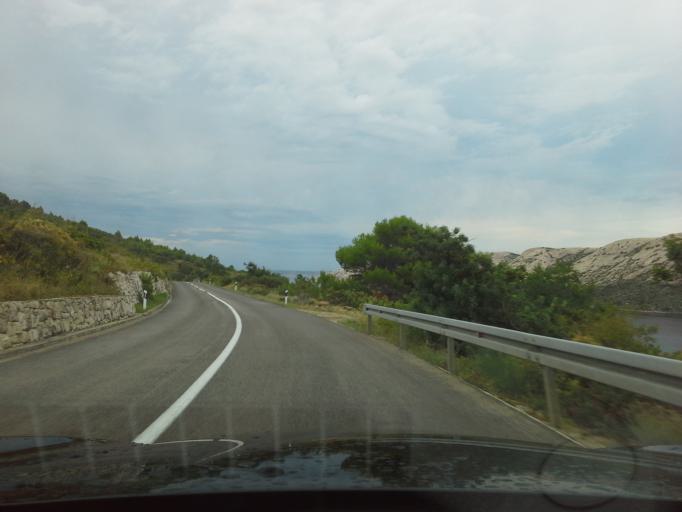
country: HR
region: Primorsko-Goranska
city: Banjol
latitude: 44.7170
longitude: 14.8249
